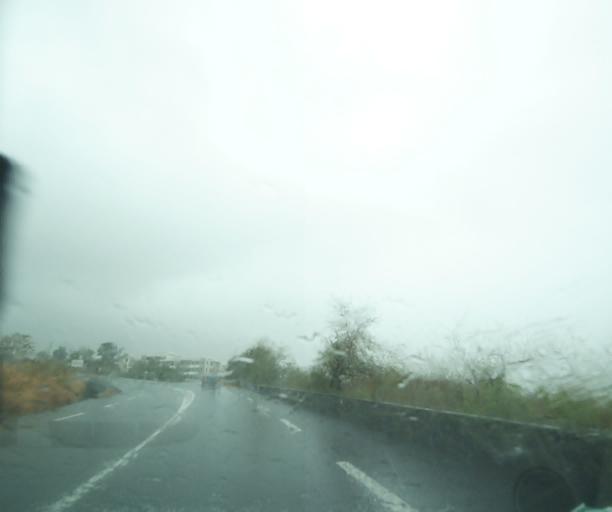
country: RE
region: Reunion
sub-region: Reunion
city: Saint-Paul
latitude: -21.0169
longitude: 55.2657
